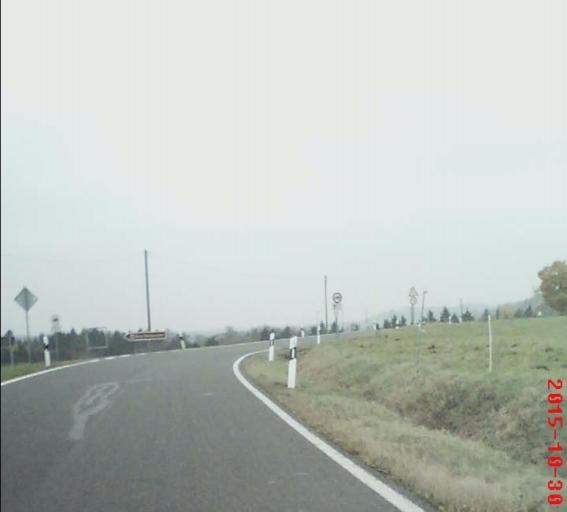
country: DE
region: Thuringia
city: Wachstedt
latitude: 51.3020
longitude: 10.2270
